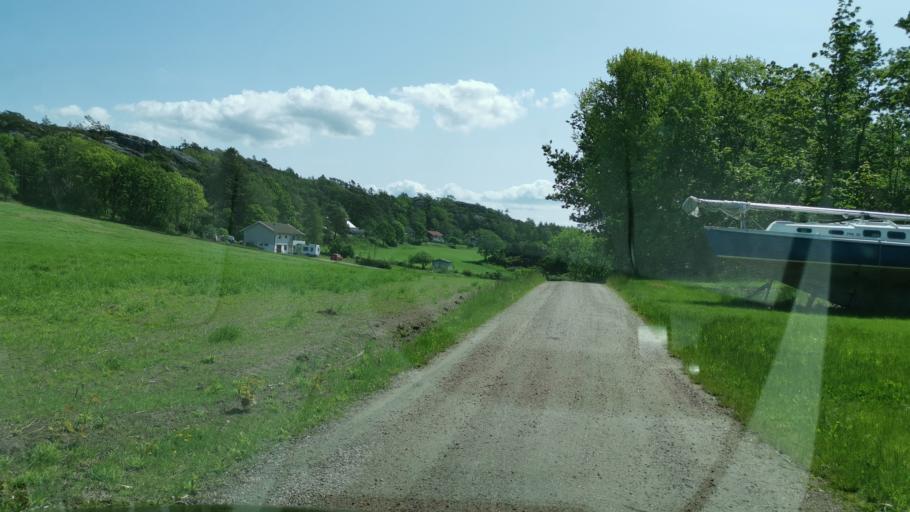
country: SE
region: Vaestra Goetaland
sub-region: Lysekils Kommun
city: Brastad
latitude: 58.3008
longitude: 11.5392
